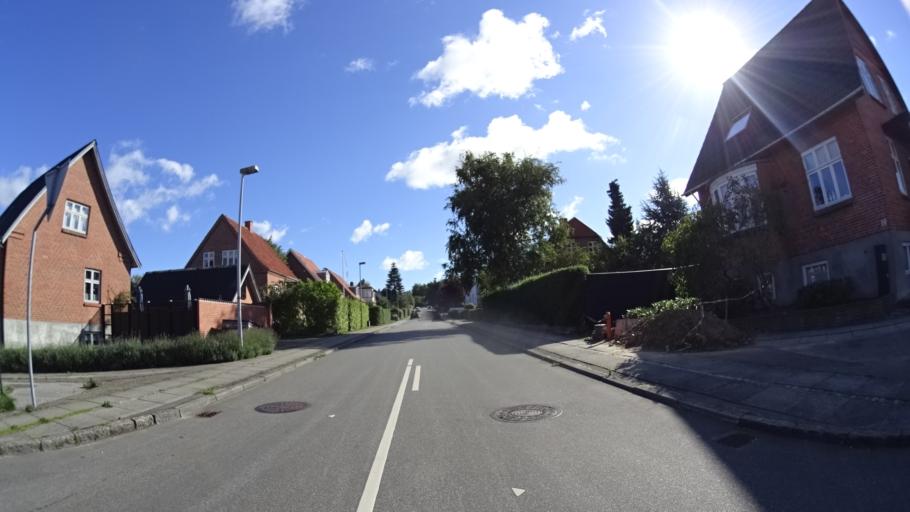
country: DK
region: Central Jutland
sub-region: Arhus Kommune
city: Stavtrup
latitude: 56.1237
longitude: 10.1583
